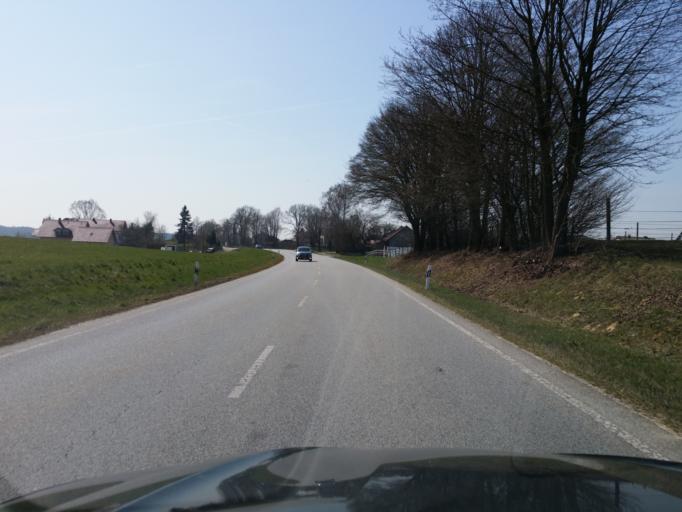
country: DE
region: Bavaria
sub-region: Lower Bavaria
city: Altfraunhofen
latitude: 48.4594
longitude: 12.1497
